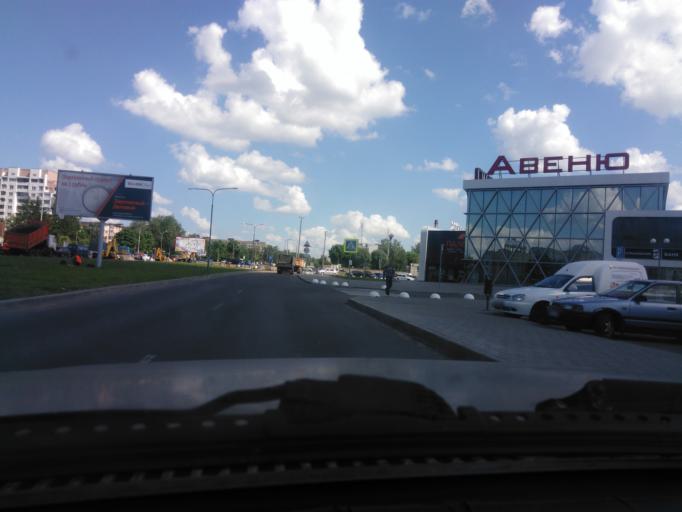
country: BY
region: Mogilev
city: Mahilyow
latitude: 53.9188
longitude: 30.2999
